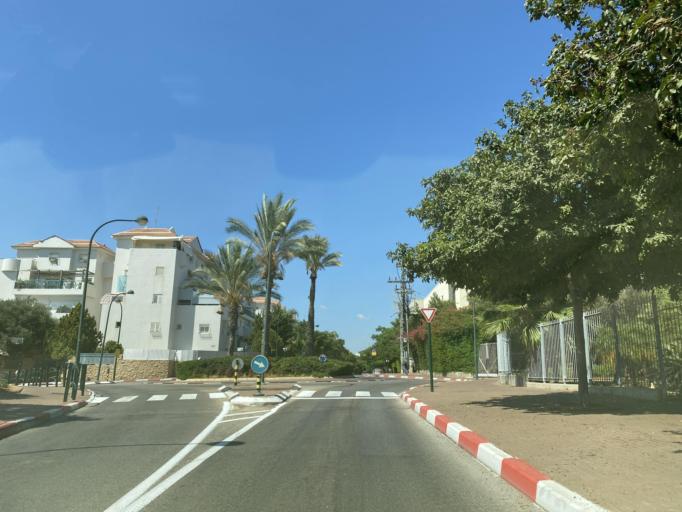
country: IL
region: Central District
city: Ra'anana
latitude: 32.1875
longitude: 34.8869
